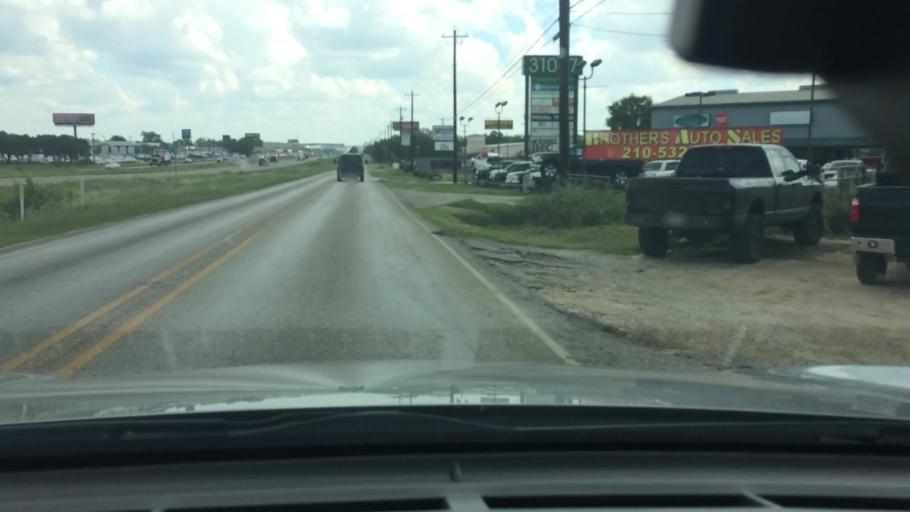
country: US
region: Texas
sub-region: Bexar County
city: Scenic Oaks
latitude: 29.7494
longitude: -98.6998
